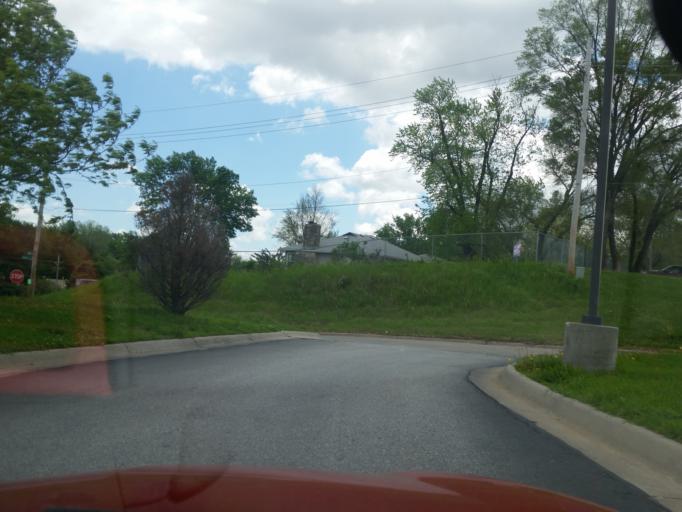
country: US
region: Nebraska
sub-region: Sarpy County
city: Bellevue
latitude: 41.1404
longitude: -95.9090
